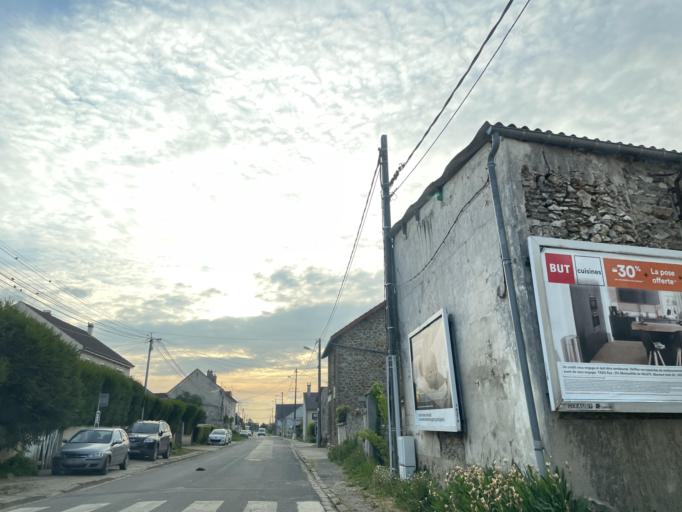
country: FR
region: Ile-de-France
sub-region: Departement de Seine-et-Marne
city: Bouleurs
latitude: 48.8912
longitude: 2.9281
